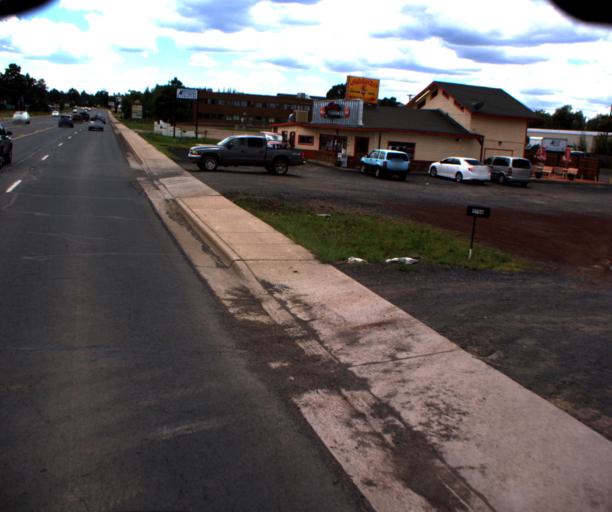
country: US
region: Arizona
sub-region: Navajo County
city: Lake of the Woods
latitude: 34.1922
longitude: -110.0157
